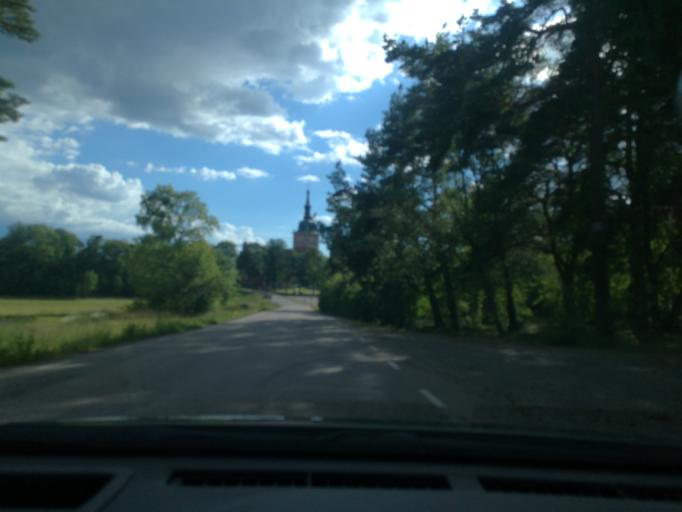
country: SE
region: Soedermanland
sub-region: Eskilstuna Kommun
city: Arla
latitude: 59.4112
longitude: 16.6945
